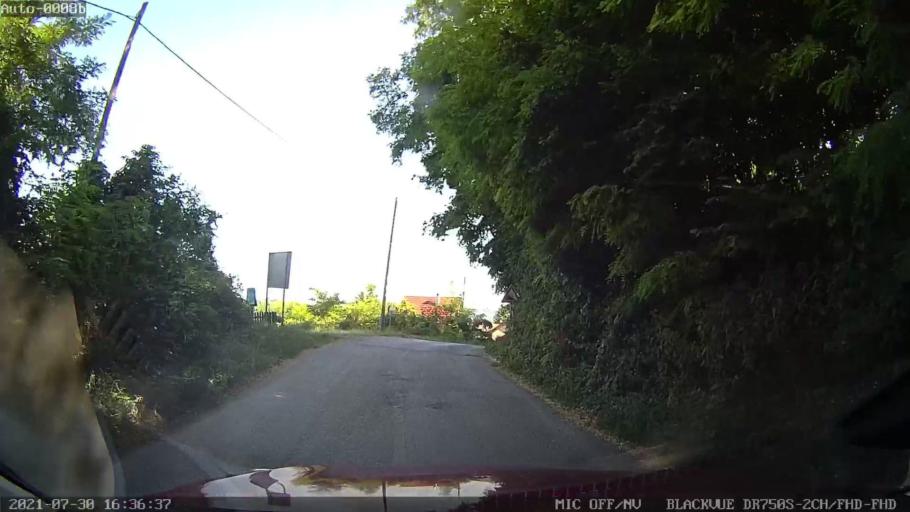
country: HR
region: Varazdinska
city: Jalzabet
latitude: 46.2393
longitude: 16.4738
